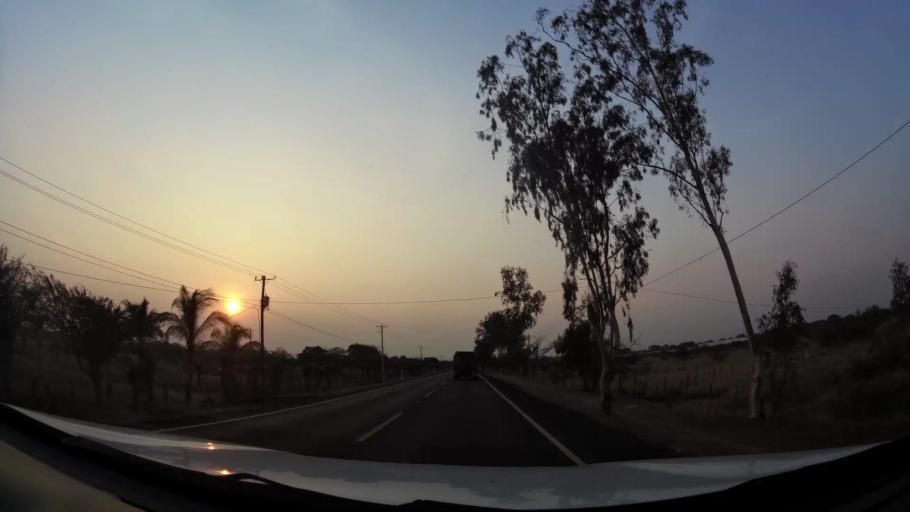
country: NI
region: Leon
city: La Paz Centro
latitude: 12.3011
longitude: -86.7732
